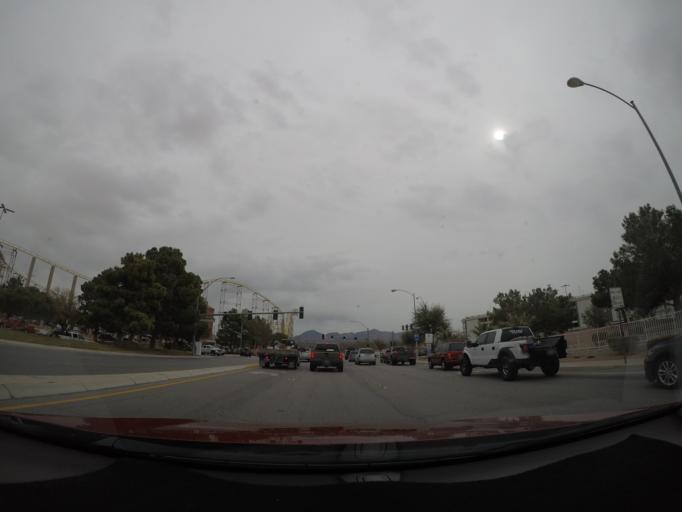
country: US
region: Nevada
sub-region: Clark County
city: Sandy Valley
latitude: 35.6123
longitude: -115.3871
